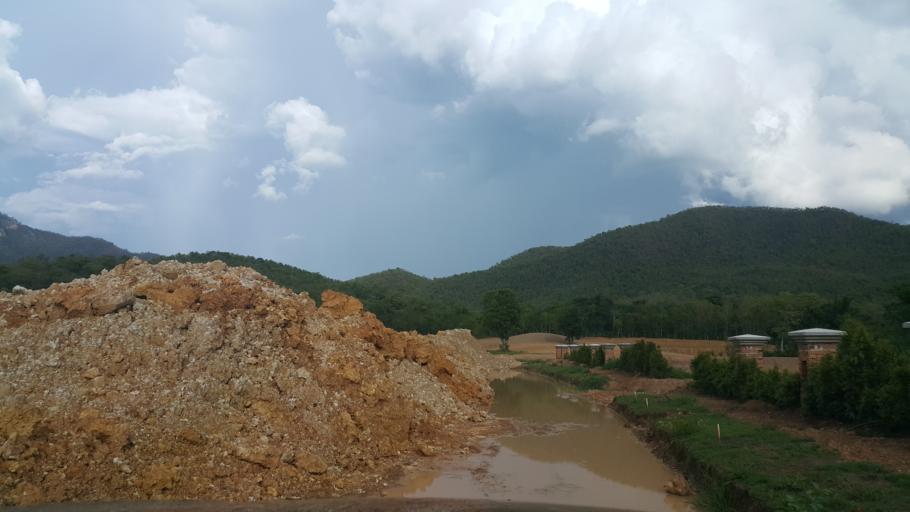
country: TH
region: Chiang Mai
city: Mae On
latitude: 18.7212
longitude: 99.2150
